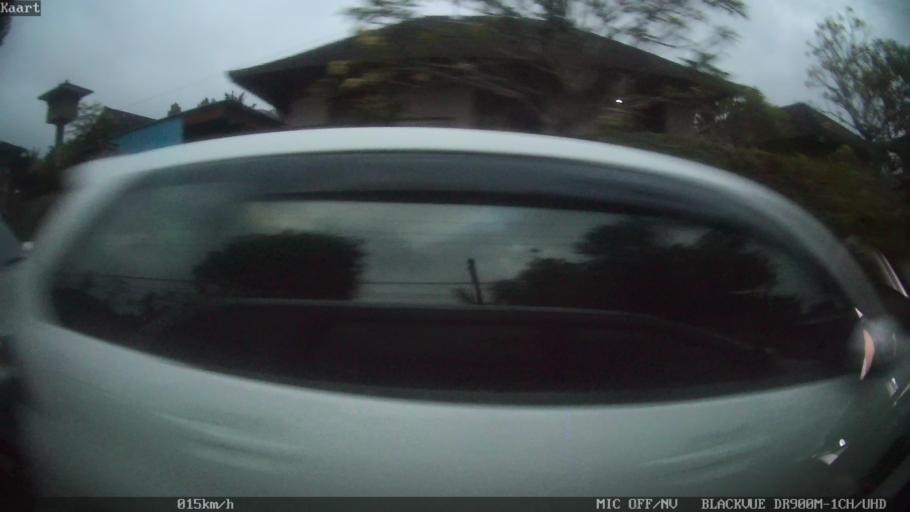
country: ID
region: Bali
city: Banjar Mambalkajanan
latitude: -8.5573
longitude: 115.2188
